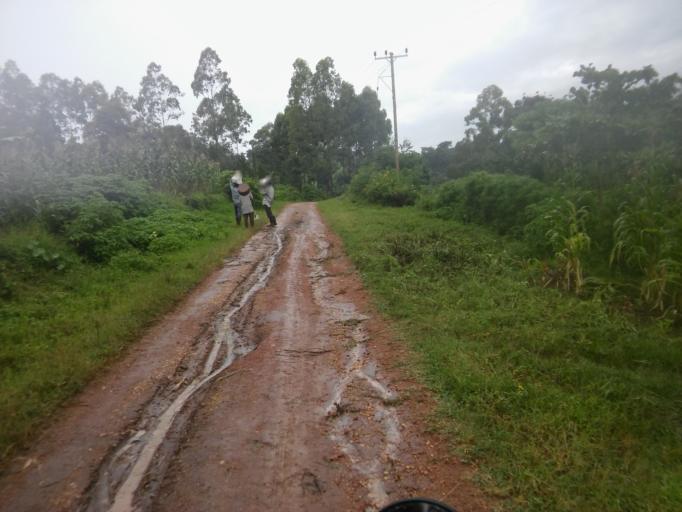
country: UG
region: Eastern Region
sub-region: Bududa District
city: Bududa
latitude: 1.0011
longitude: 34.2415
